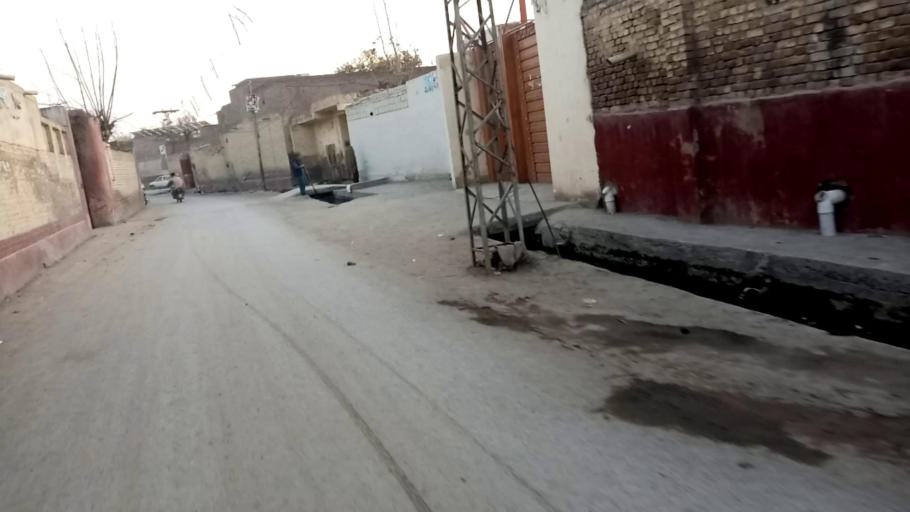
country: PK
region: Khyber Pakhtunkhwa
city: Peshawar
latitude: 34.0499
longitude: 71.4599
